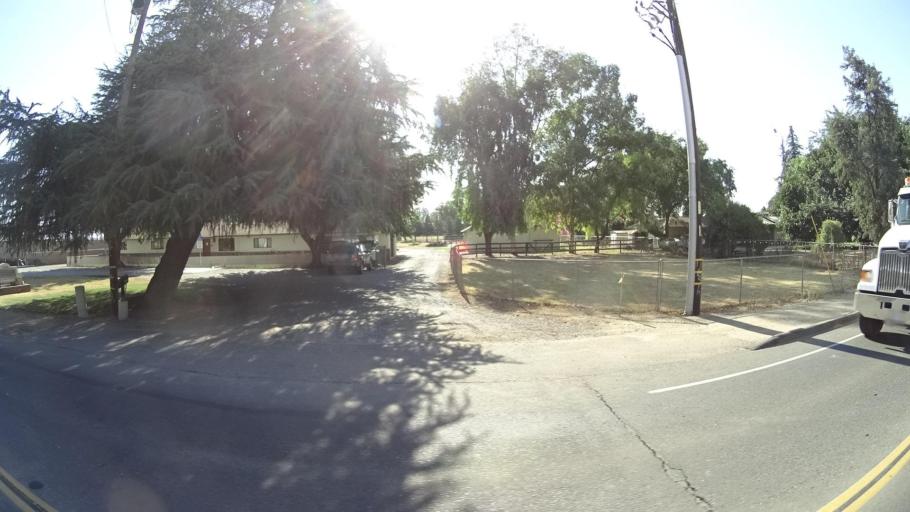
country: US
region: California
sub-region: Fresno County
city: Tarpey Village
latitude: 36.7736
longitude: -119.6641
